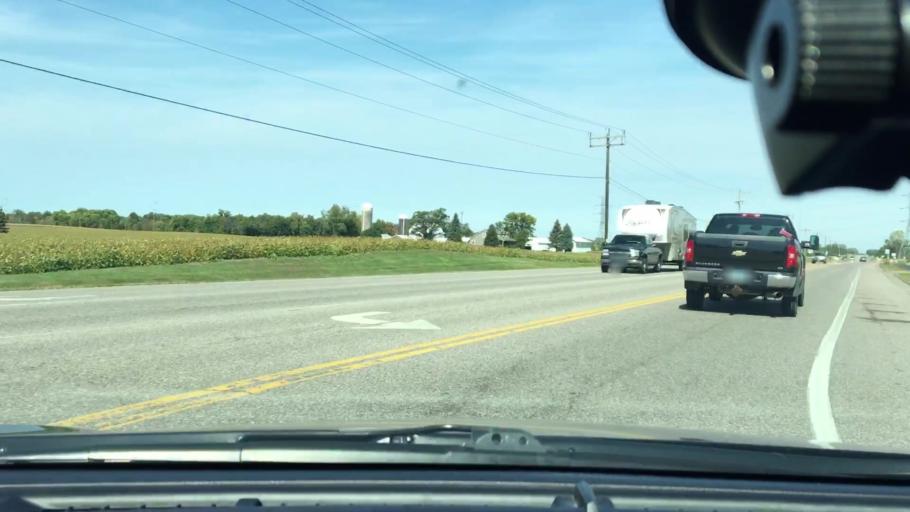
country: US
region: Minnesota
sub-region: Wright County
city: Hanover
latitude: 45.1238
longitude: -93.6358
